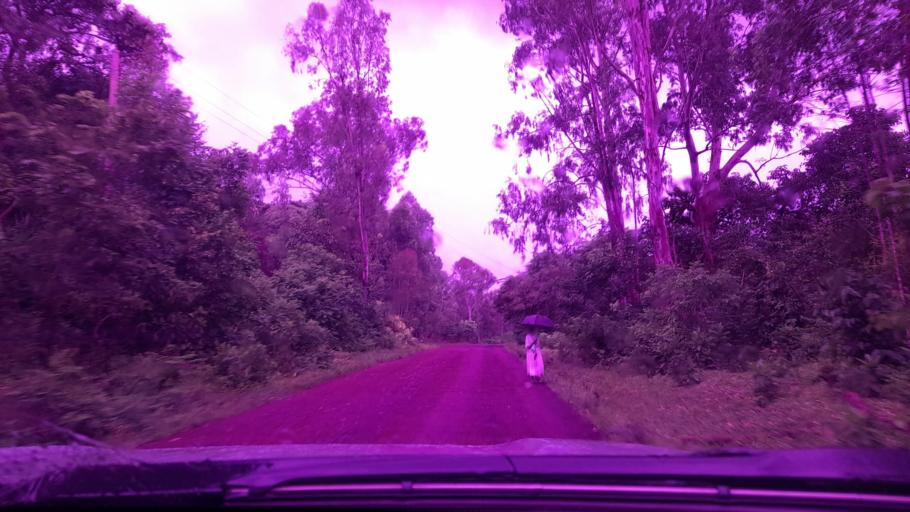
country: ET
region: Oromiya
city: Metu
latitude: 8.4450
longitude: 35.6261
